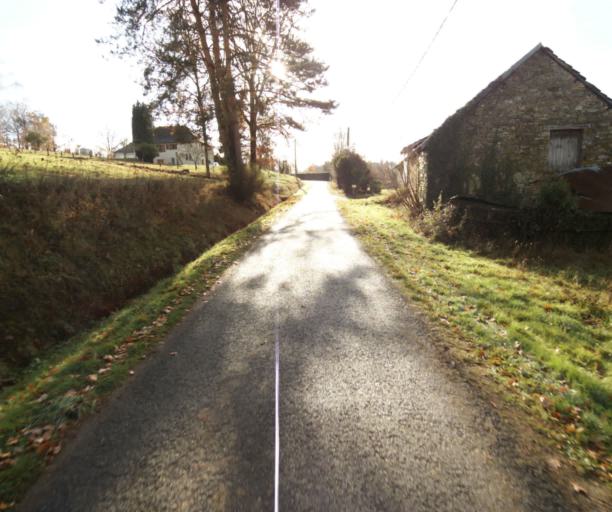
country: FR
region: Limousin
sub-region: Departement de la Correze
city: Saint-Mexant
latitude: 45.2593
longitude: 1.6286
